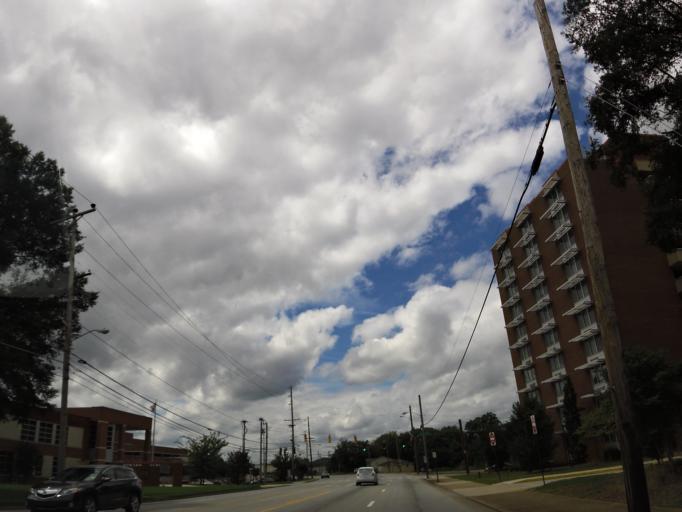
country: US
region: Tennessee
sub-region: Hamilton County
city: Chattanooga
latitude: 35.0264
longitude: -85.3112
